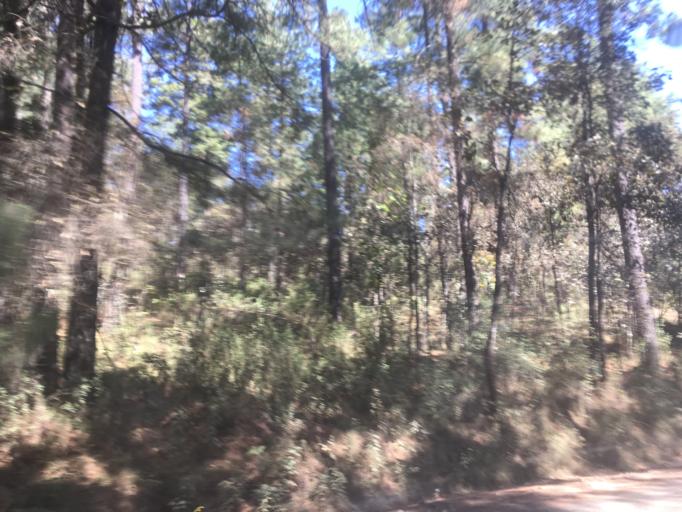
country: MX
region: Michoacan
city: Angahuan
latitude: 19.4894
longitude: -102.2056
